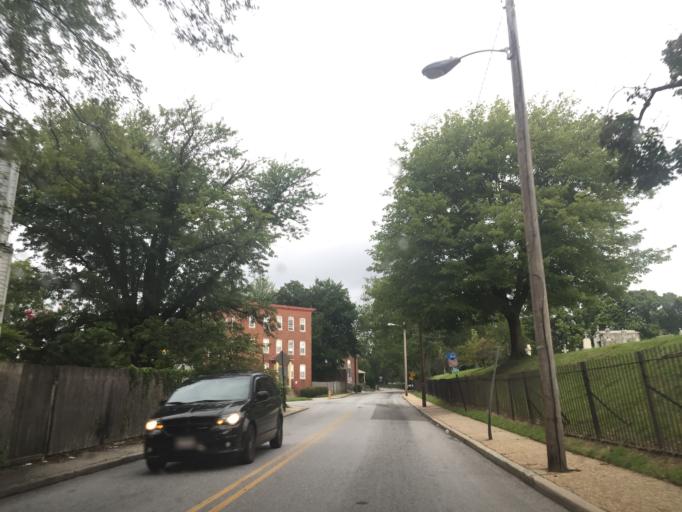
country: US
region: Maryland
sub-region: Baltimore County
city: Charlestown
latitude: 39.2858
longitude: -76.6842
